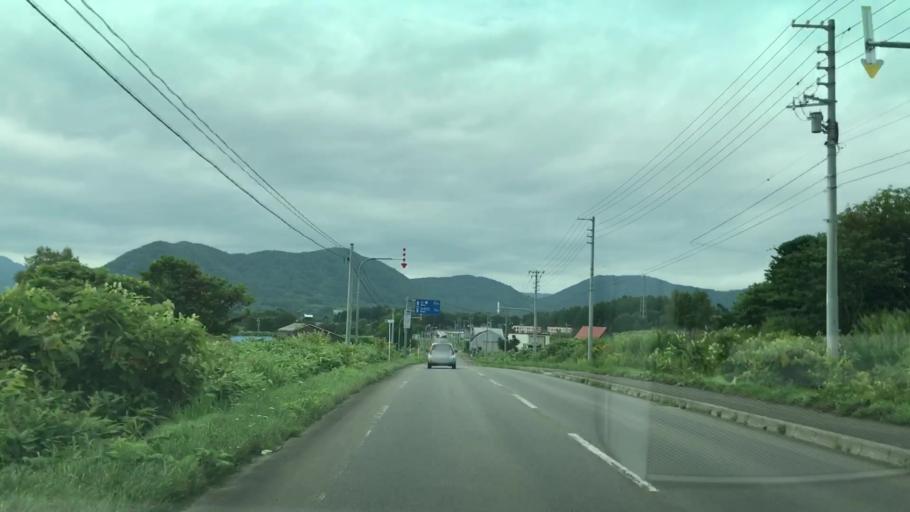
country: JP
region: Hokkaido
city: Yoichi
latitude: 43.0945
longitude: 140.8200
